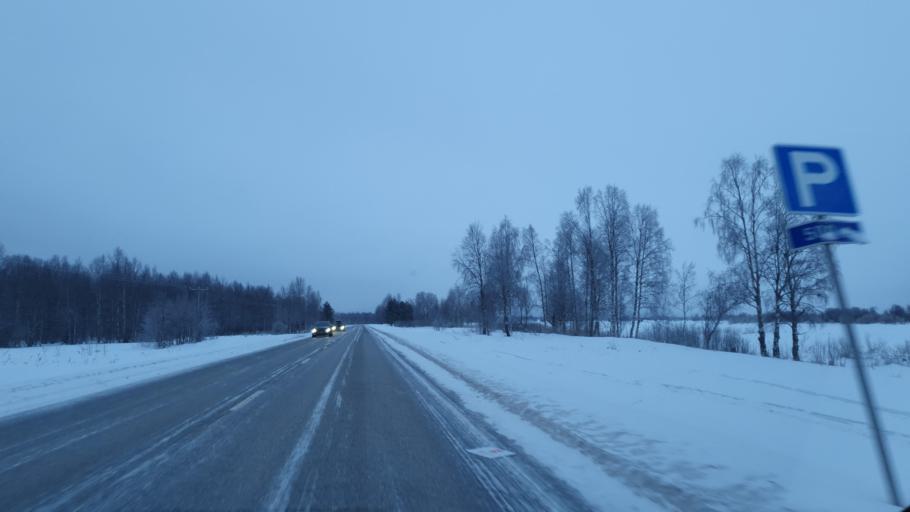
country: SE
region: Norrbotten
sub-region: Overtornea Kommun
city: OEvertornea
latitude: 66.3973
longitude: 23.6826
